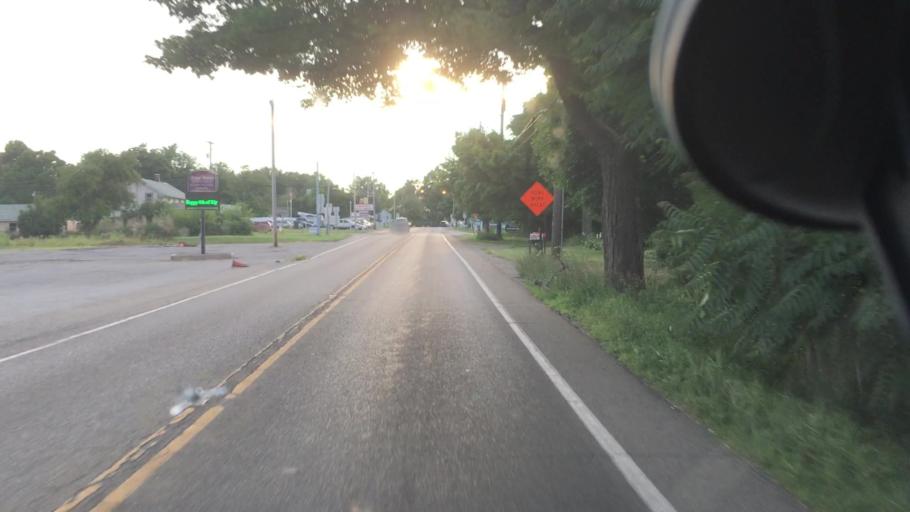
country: US
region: Ohio
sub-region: Columbiana County
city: East Palestine
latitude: 40.8645
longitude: -80.5567
